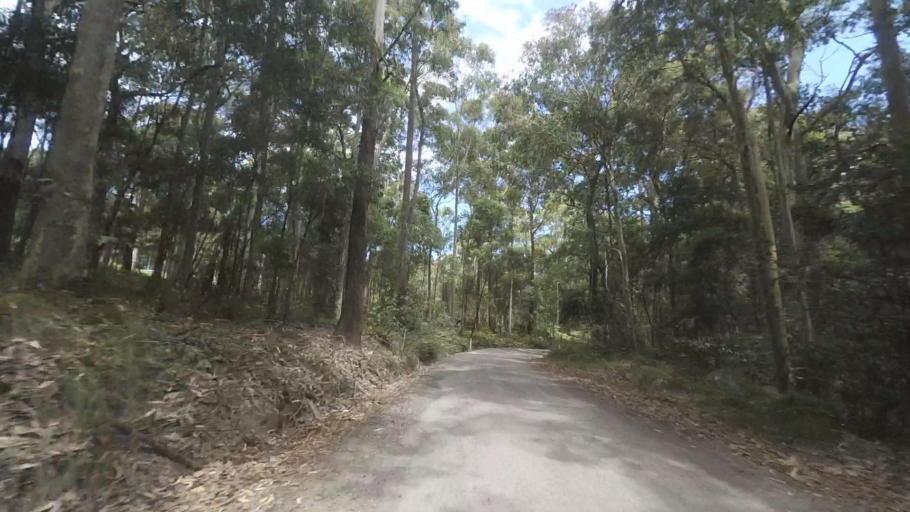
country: AU
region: New South Wales
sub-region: Shoalhaven Shire
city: Milton
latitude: -35.4429
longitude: 150.3123
